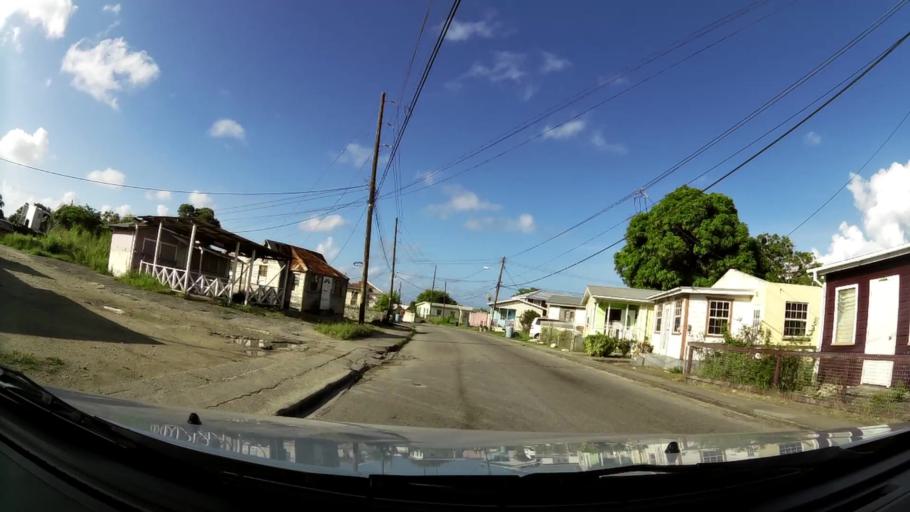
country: BB
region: Saint Michael
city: Bridgetown
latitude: 13.1078
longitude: -59.5957
